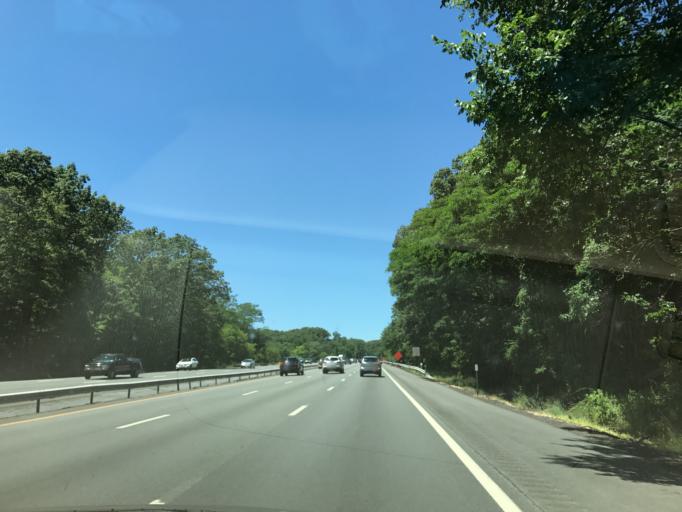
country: US
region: New York
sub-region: Rockland County
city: Monsey
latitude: 41.1029
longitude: -74.0719
